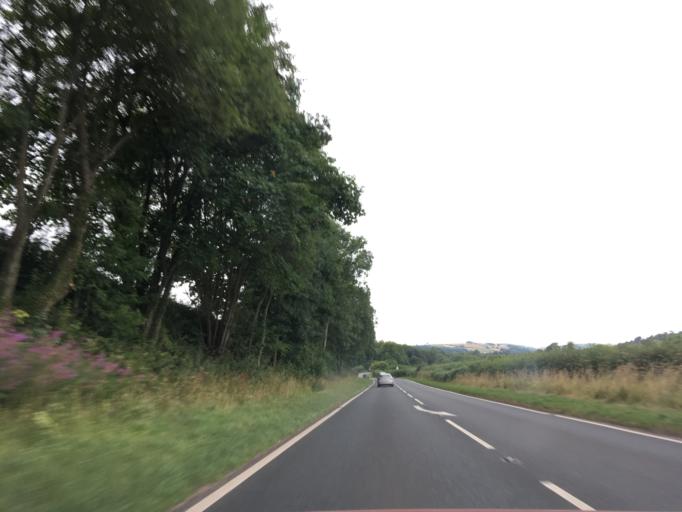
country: GB
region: Wales
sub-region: Sir Powys
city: Brecon
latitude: 51.9484
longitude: -3.4764
